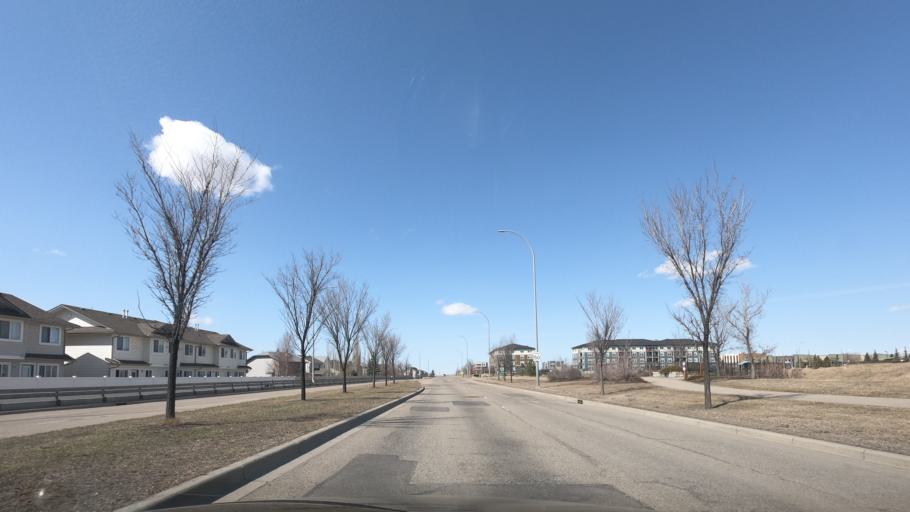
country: CA
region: Alberta
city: Airdrie
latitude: 51.3022
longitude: -114.0133
